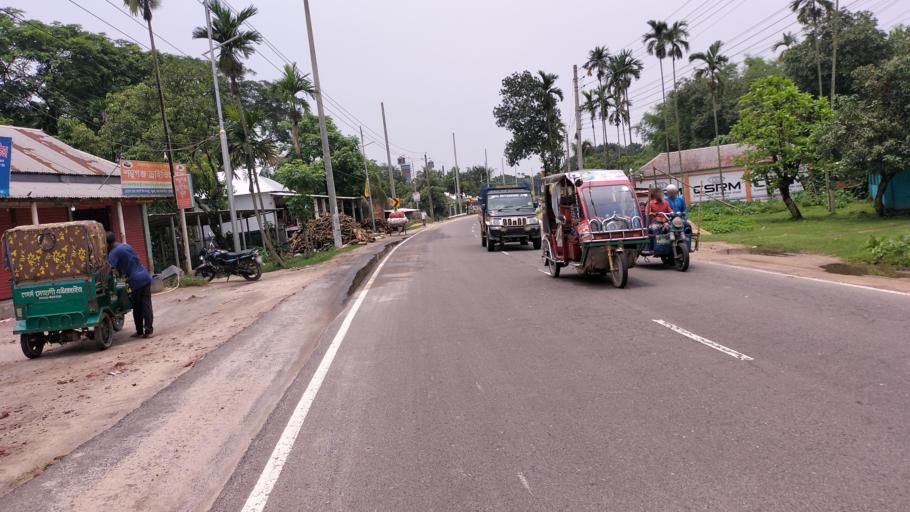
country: BD
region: Dhaka
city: Mymensingh
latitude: 24.7709
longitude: 90.4562
